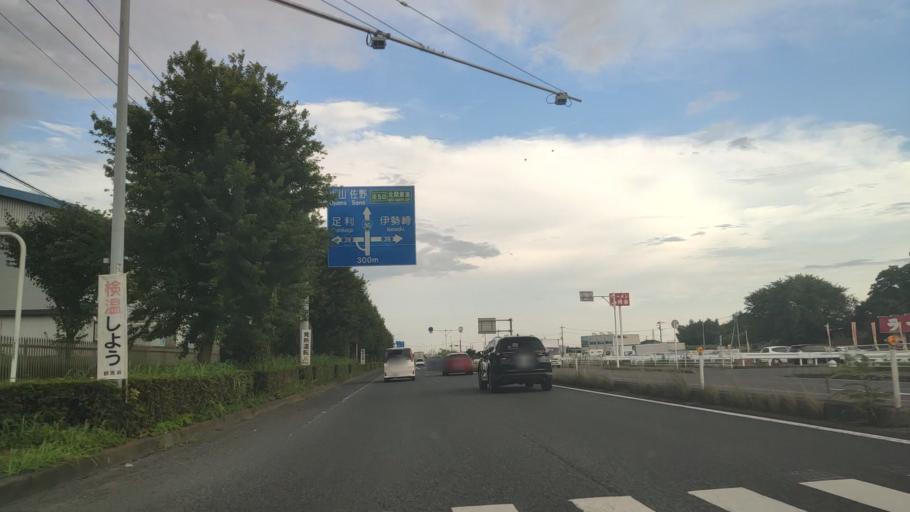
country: JP
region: Gunma
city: Ota
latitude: 36.3439
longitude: 139.3835
